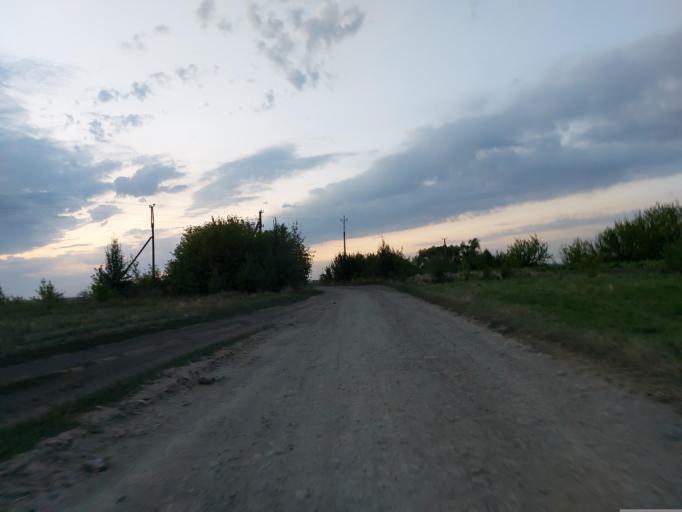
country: RU
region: Lipetsk
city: Dolgorukovo
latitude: 52.3799
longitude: 38.0447
